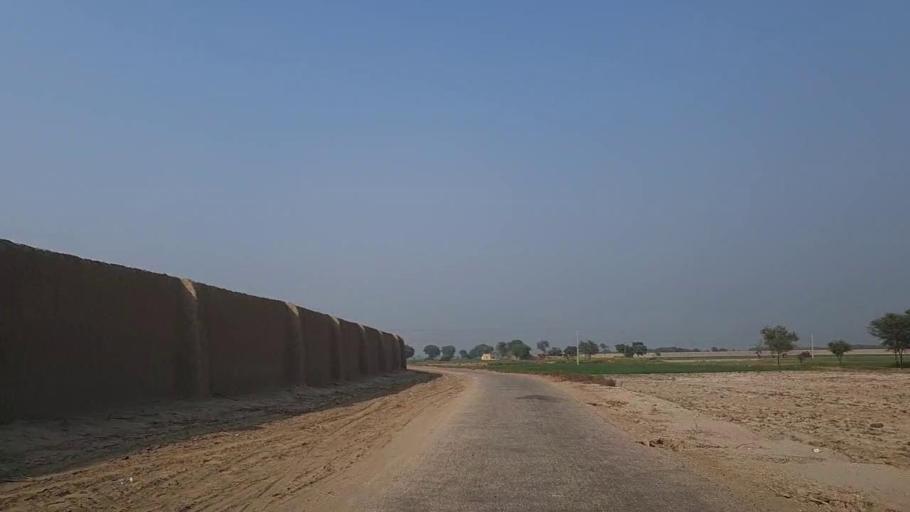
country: PK
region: Sindh
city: Sann
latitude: 26.1089
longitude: 68.1758
